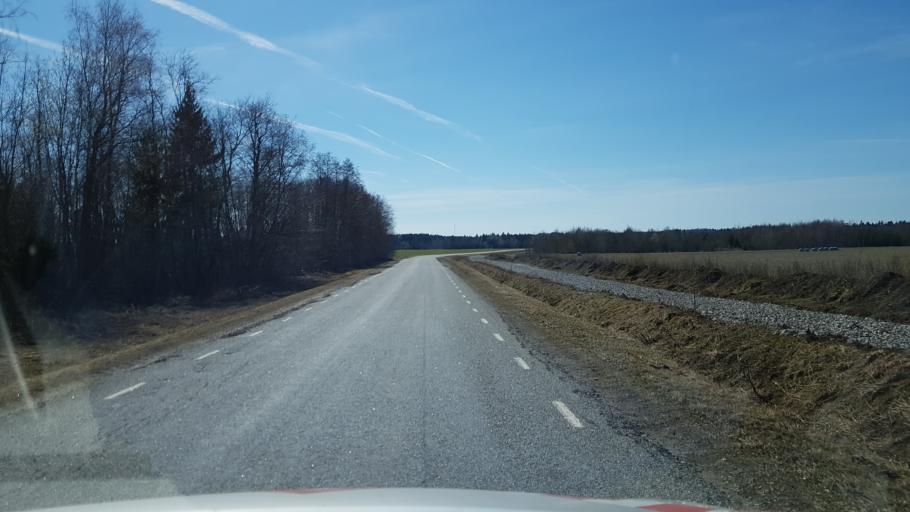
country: EE
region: Laeaene-Virumaa
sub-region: Viru-Nigula vald
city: Kunda
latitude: 59.3368
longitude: 26.6516
